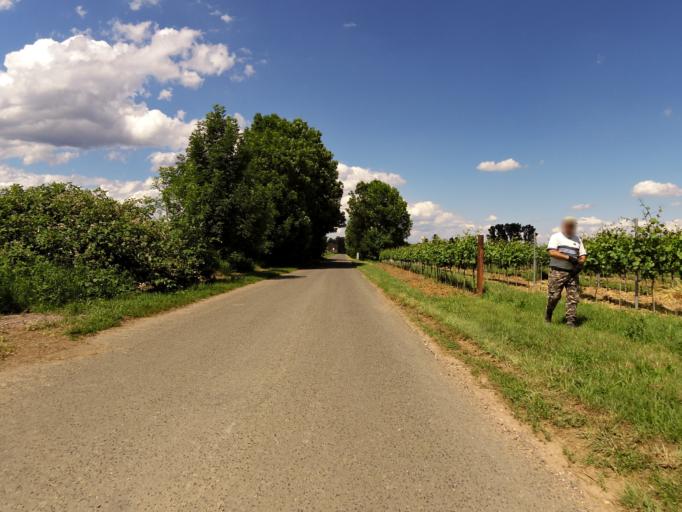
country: DE
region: Rheinland-Pfalz
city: Altdorf
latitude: 49.2931
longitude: 8.2147
